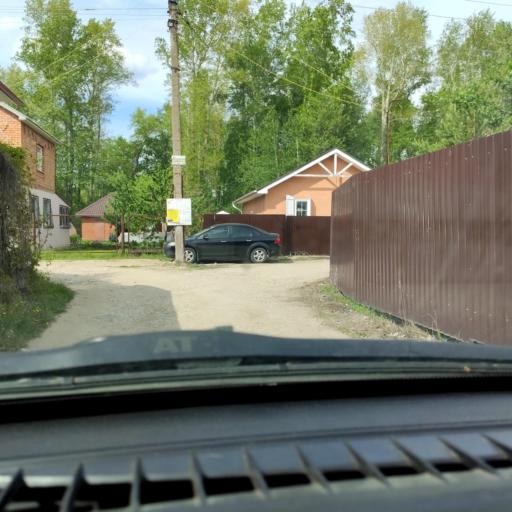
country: RU
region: Samara
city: Zhigulevsk
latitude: 53.4590
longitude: 49.5185
